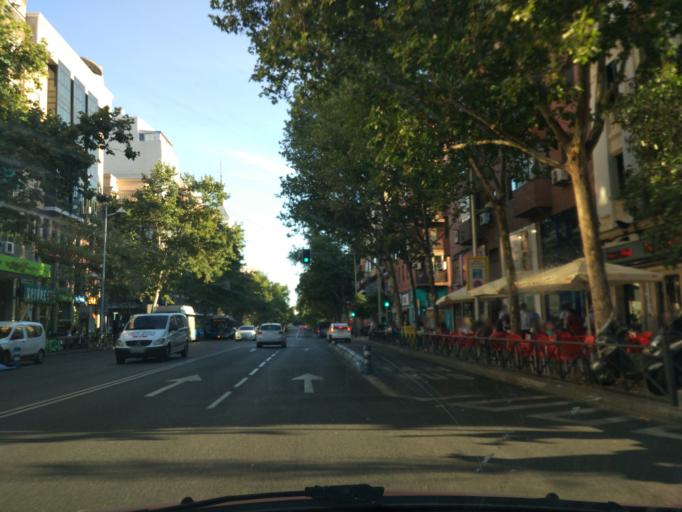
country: ES
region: Madrid
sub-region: Provincia de Madrid
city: Chamberi
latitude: 40.4524
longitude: -3.7032
